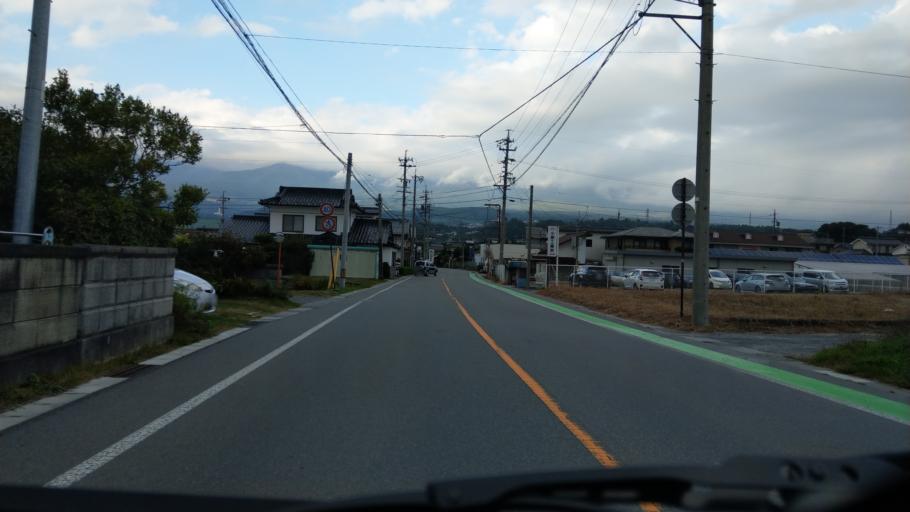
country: JP
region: Nagano
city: Komoro
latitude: 36.3132
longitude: 138.4306
